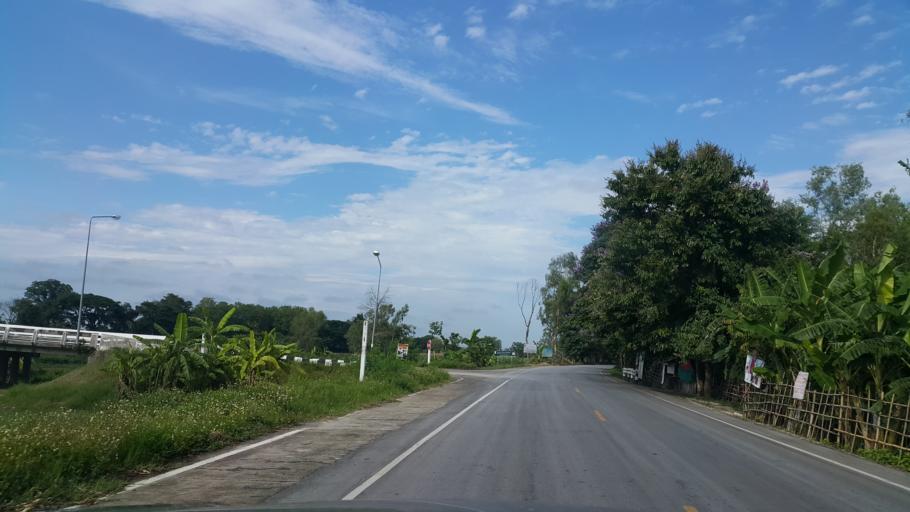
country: TH
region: Chiang Rai
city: Wiang Chai
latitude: 19.9592
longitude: 99.9460
